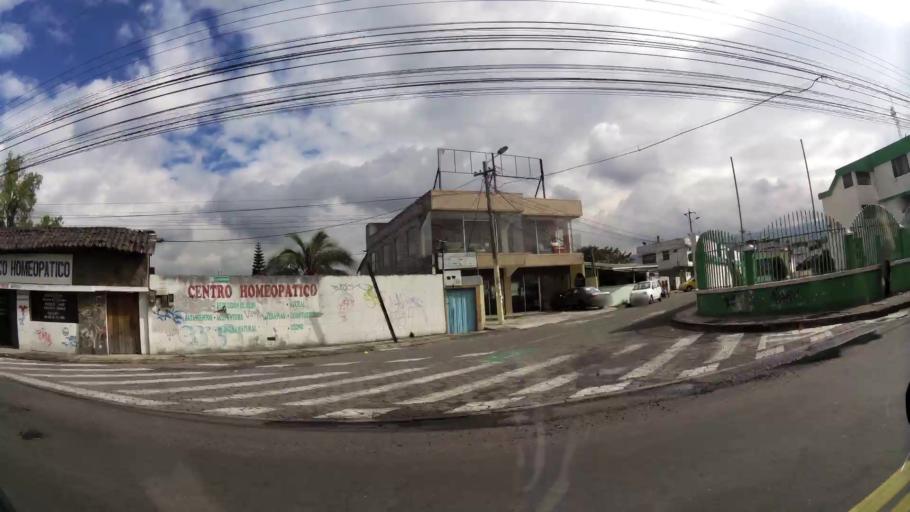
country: EC
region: Pichincha
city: Sangolqui
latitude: -0.3069
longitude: -78.4544
